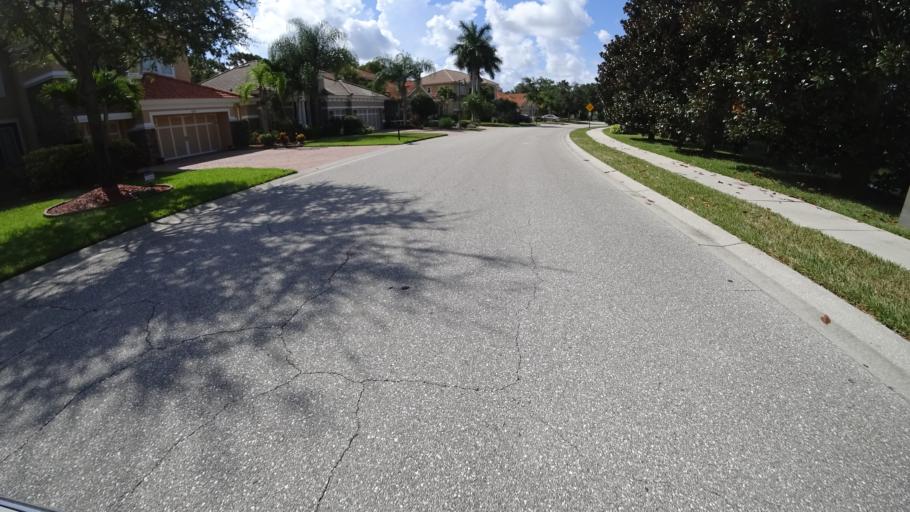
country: US
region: Florida
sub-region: Sarasota County
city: Desoto Lakes
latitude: 27.3935
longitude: -82.4965
